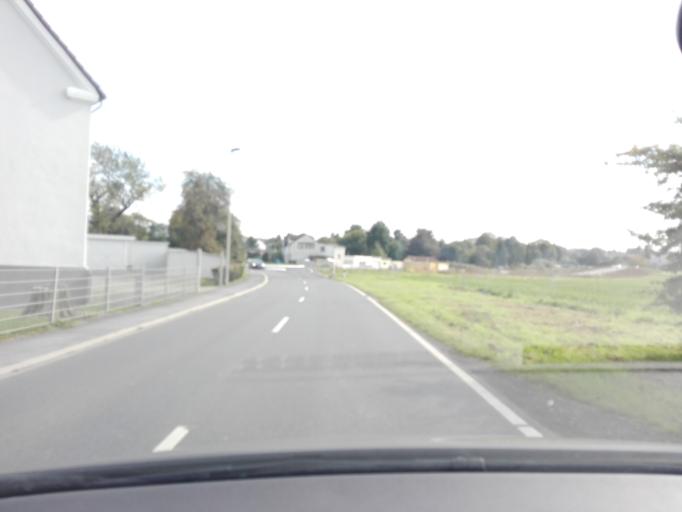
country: DE
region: North Rhine-Westphalia
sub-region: Regierungsbezirk Arnsberg
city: Unna
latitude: 51.5460
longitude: 7.6681
